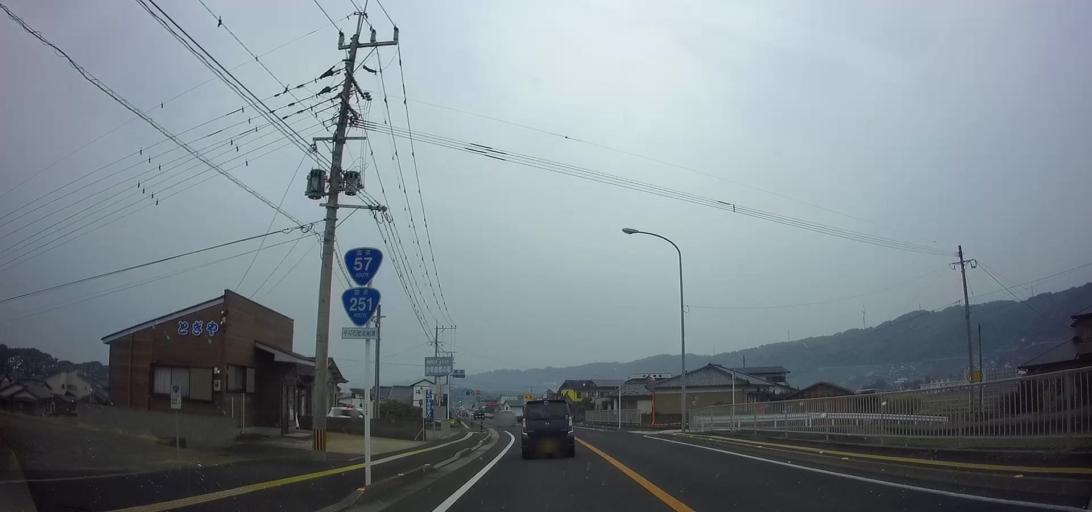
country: JP
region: Nagasaki
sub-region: Isahaya-shi
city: Isahaya
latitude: 32.7870
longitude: 130.1949
